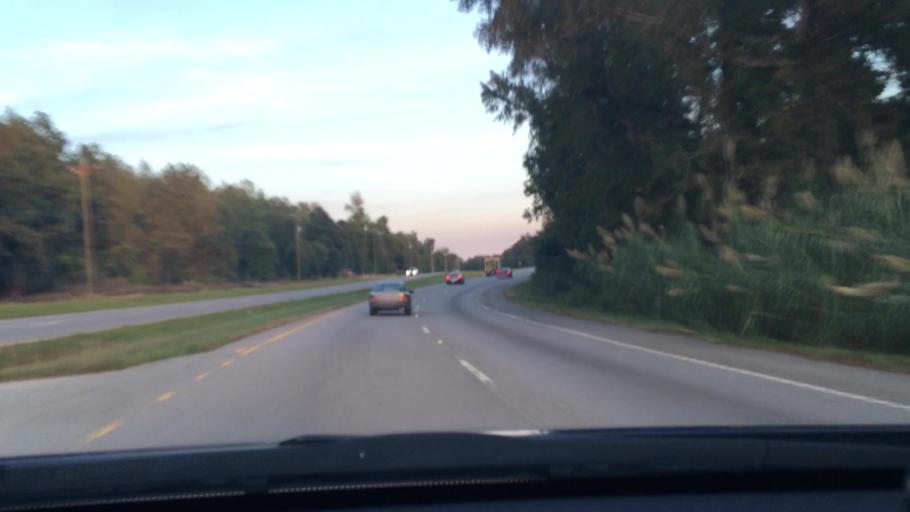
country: US
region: South Carolina
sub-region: Richland County
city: Gadsden
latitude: 33.9430
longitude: -80.7765
